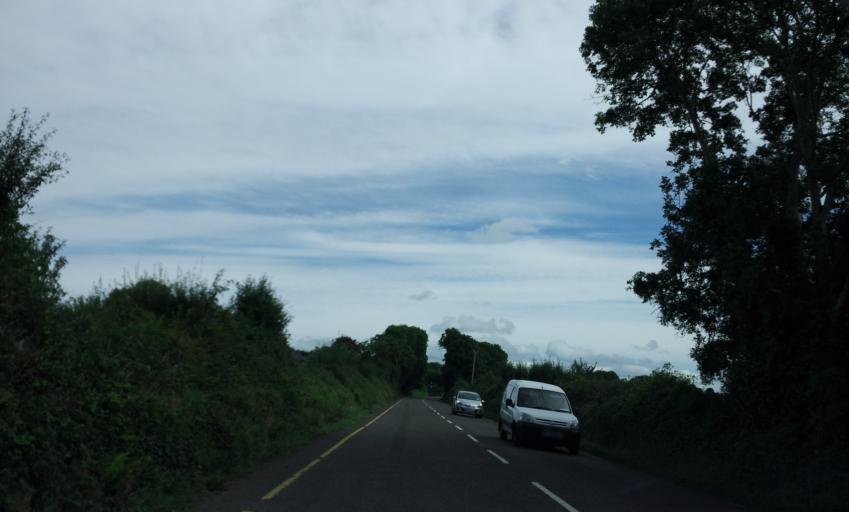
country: IE
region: Munster
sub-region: Ciarrai
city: Killorglin
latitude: 52.1016
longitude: -9.7665
